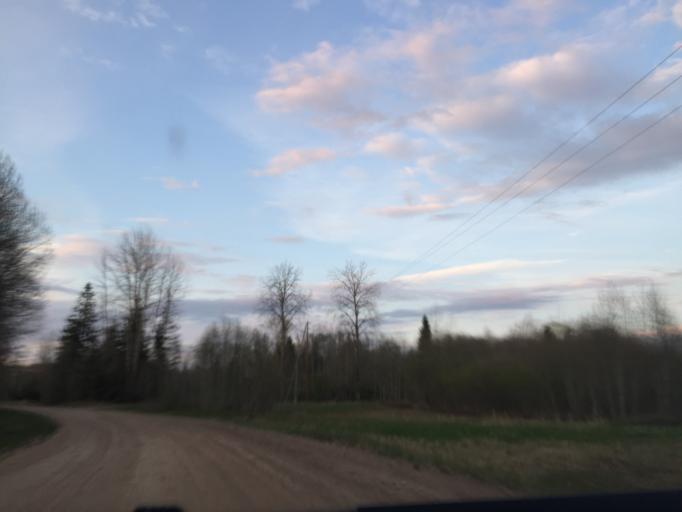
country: LV
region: Aluksnes Rajons
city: Aluksne
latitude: 57.2910
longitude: 26.9167
